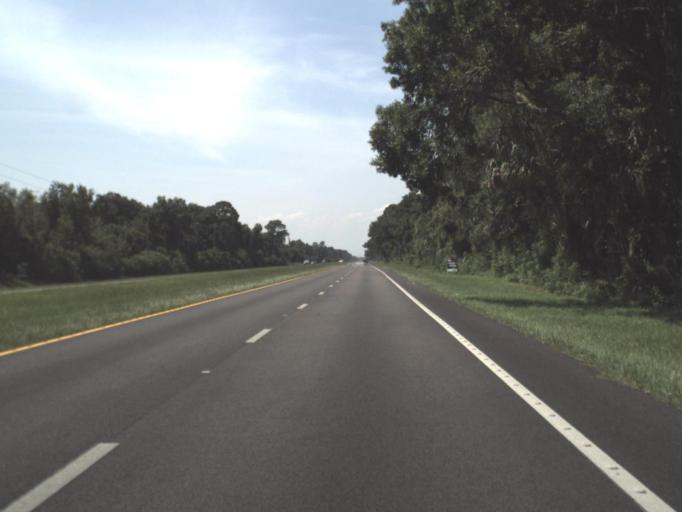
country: US
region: Florida
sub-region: Citrus County
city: Crystal River
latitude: 28.9300
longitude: -82.6155
